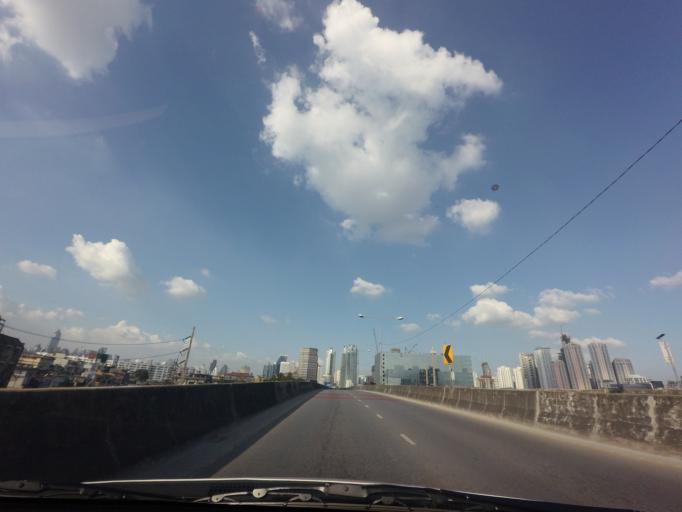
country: TH
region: Bangkok
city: Khlong Toei
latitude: 13.7179
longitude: 100.5582
